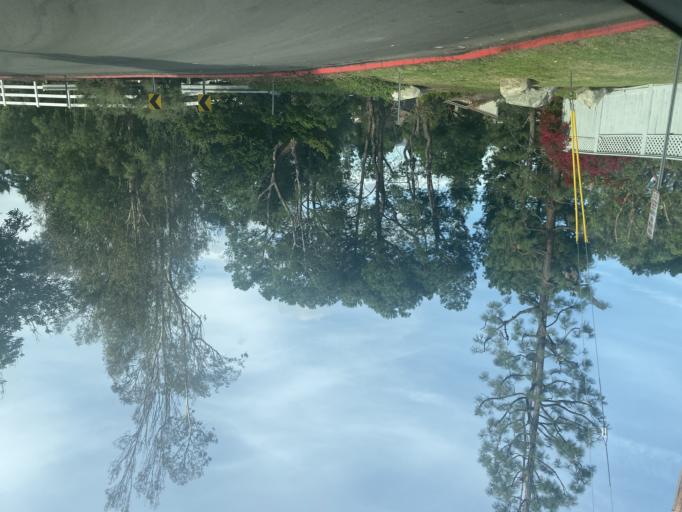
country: US
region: California
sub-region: Orange County
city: Placentia
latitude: 33.8908
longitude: -117.8879
